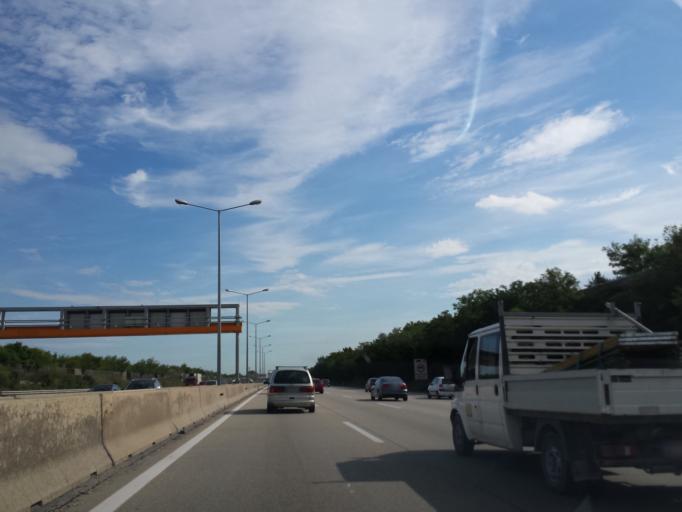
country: AT
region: Lower Austria
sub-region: Politischer Bezirk Modling
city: Wiener Neudorf
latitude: 48.0917
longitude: 16.3267
